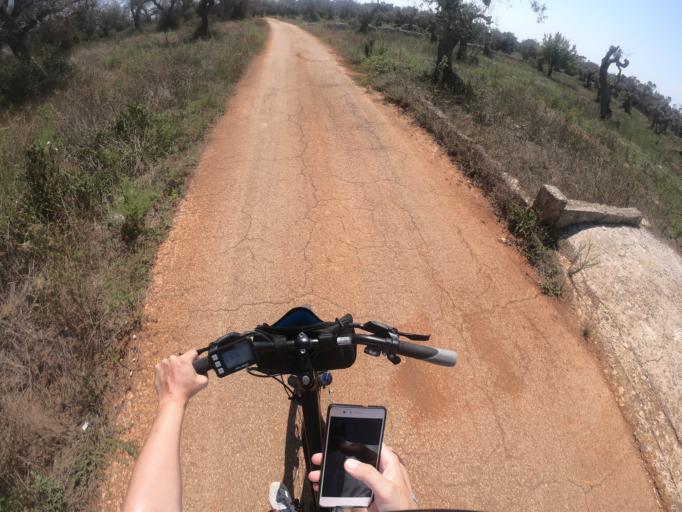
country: IT
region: Apulia
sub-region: Provincia di Lecce
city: Specchia
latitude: 39.9295
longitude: 18.2752
